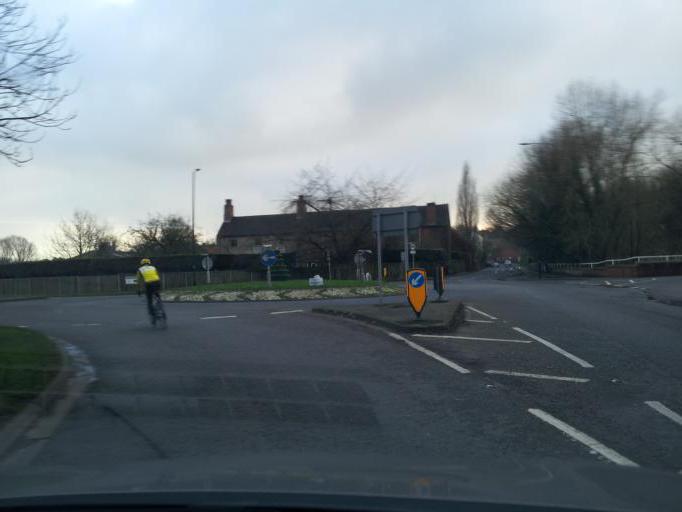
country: GB
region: England
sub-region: Staffordshire
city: Burton upon Trent
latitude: 52.8615
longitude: -1.6831
